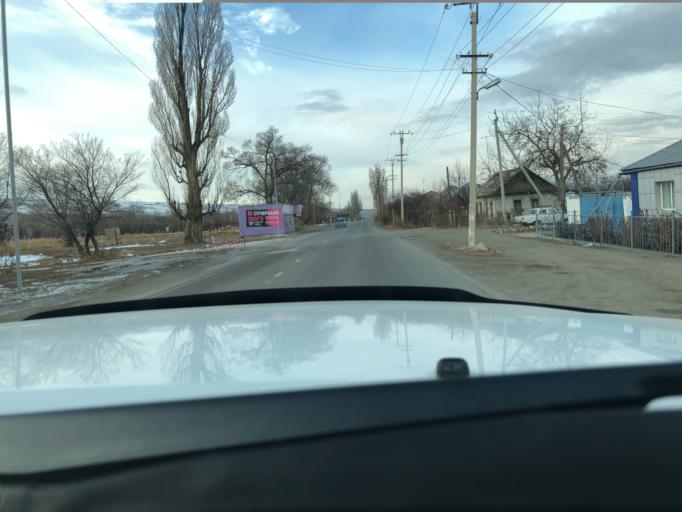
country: KG
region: Ysyk-Koel
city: Karakol
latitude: 42.4700
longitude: 78.3804
